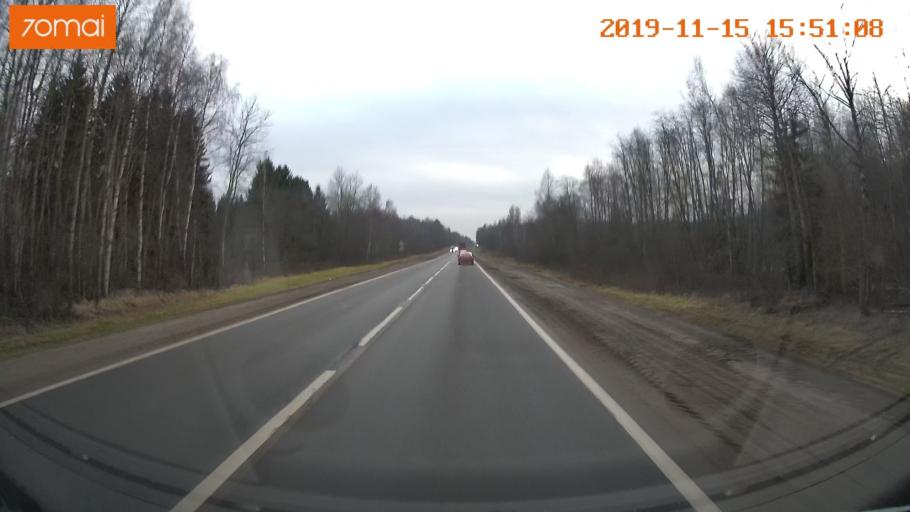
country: RU
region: Jaroslavl
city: Yaroslavl
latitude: 57.8982
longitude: 40.0098
